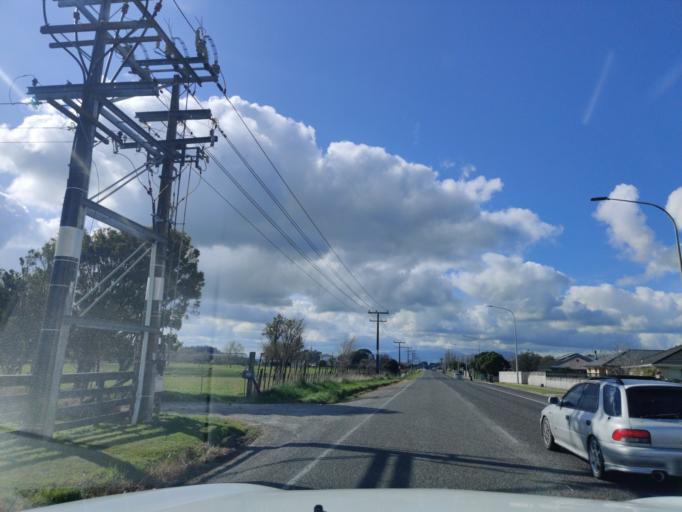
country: NZ
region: Manawatu-Wanganui
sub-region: Palmerston North City
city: Palmerston North
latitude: -40.3203
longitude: 175.6530
